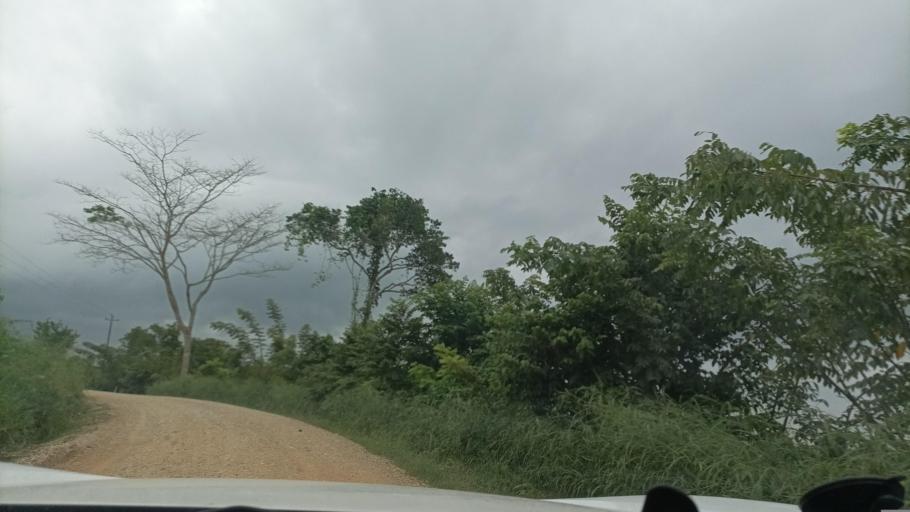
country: MX
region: Veracruz
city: Hidalgotitlan
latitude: 17.6522
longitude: -94.4992
